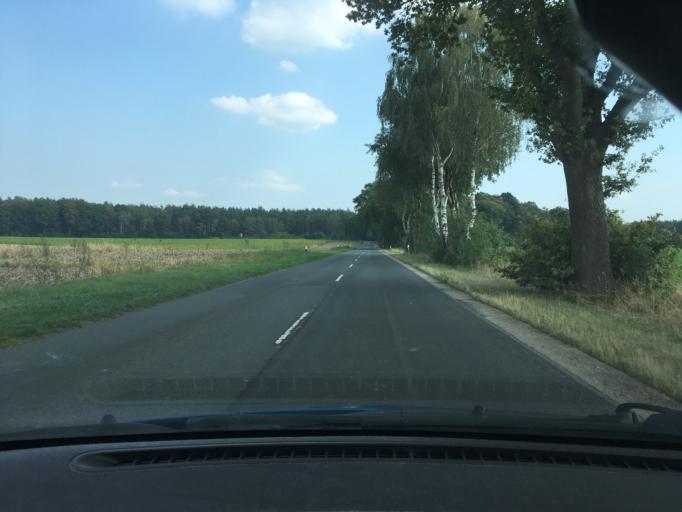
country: DE
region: Lower Saxony
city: Oldendorf
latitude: 53.1548
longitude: 10.2644
